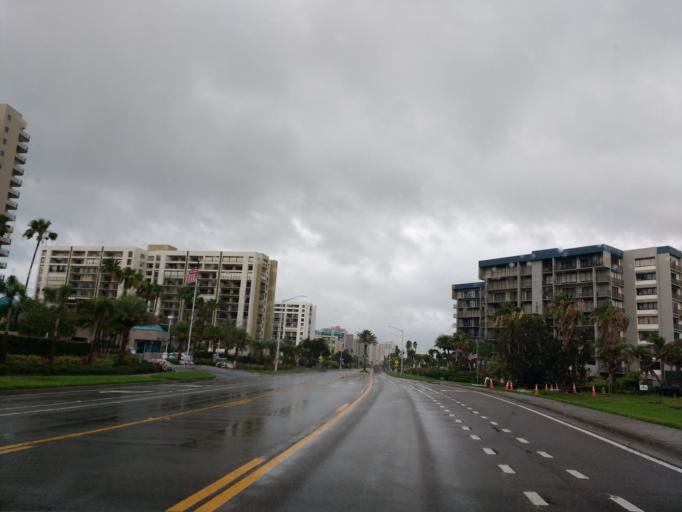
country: US
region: Florida
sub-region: Pinellas County
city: Belleair Beach
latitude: 27.9416
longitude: -82.8365
